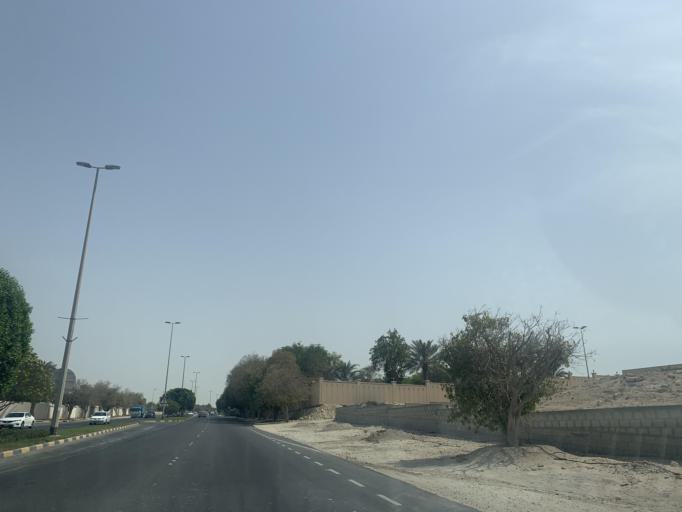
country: BH
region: Northern
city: Ar Rifa'
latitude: 26.1486
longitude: 50.5423
